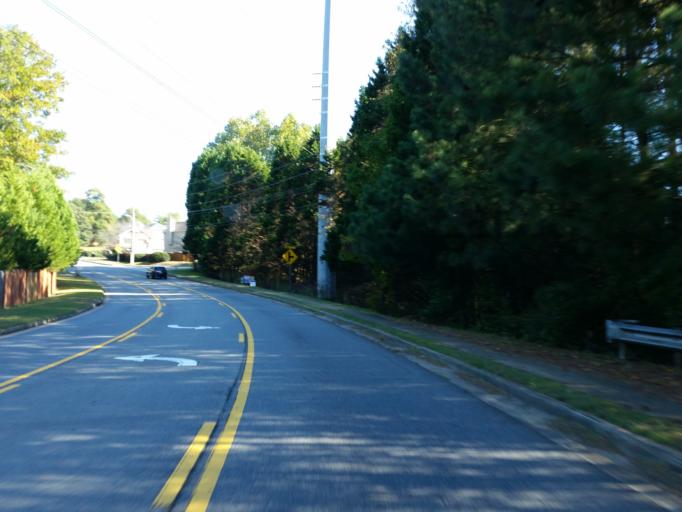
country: US
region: Georgia
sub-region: Cobb County
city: Marietta
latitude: 34.0138
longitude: -84.4823
